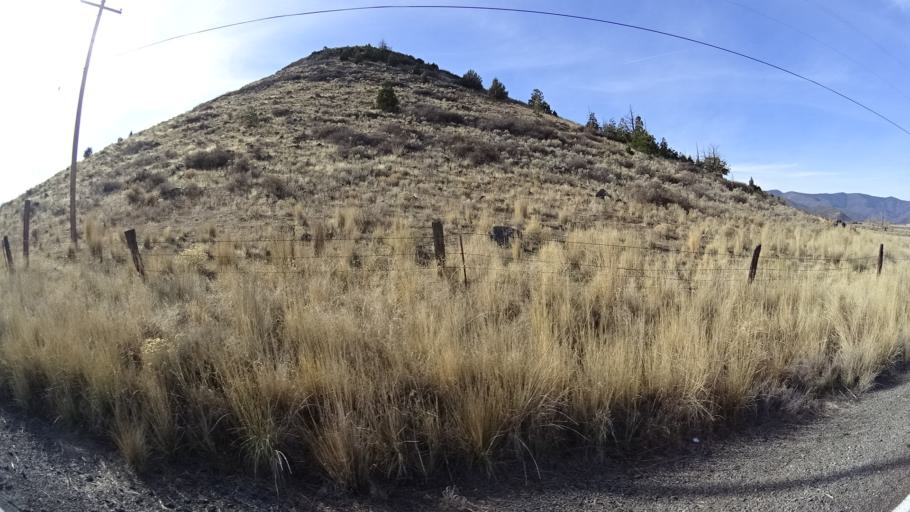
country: US
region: California
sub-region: Siskiyou County
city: Weed
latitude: 41.5361
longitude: -122.5201
